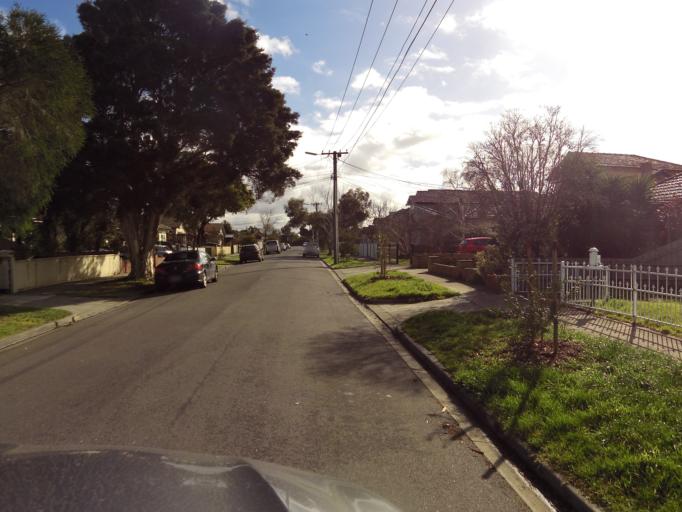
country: AU
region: Victoria
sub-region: Maribyrnong
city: Kingsville
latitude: -37.8139
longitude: 144.8757
